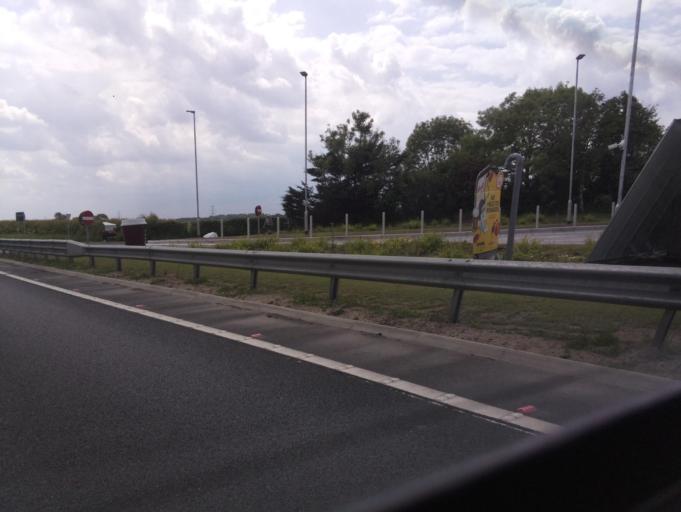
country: GB
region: England
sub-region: Stockton-on-Tees
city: Yarm
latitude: 54.4042
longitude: -1.3200
